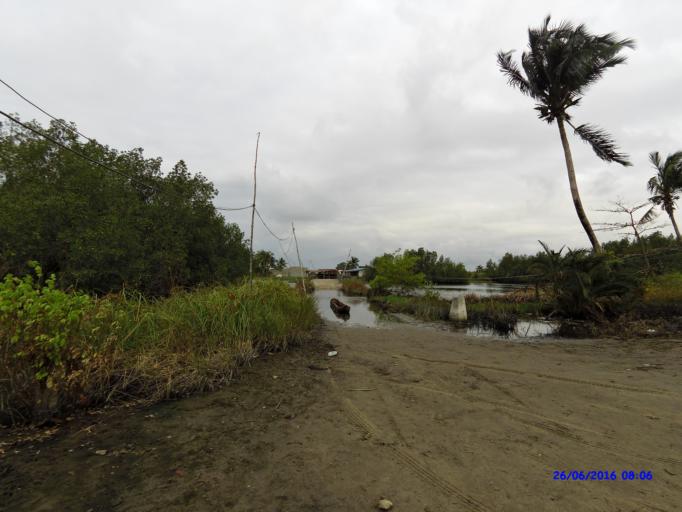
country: BJ
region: Atlantique
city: Hevie
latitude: 6.3577
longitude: 2.3124
